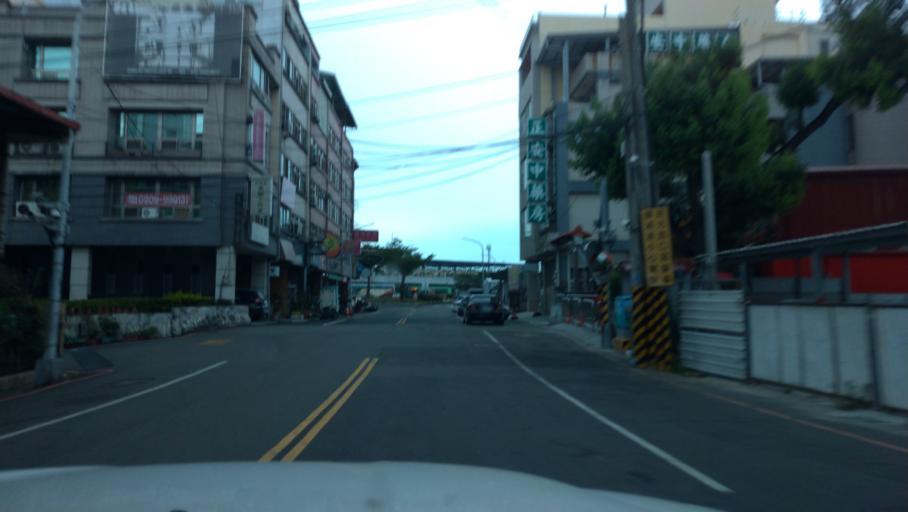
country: TW
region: Taiwan
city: Fengyuan
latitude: 24.2532
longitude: 120.7252
